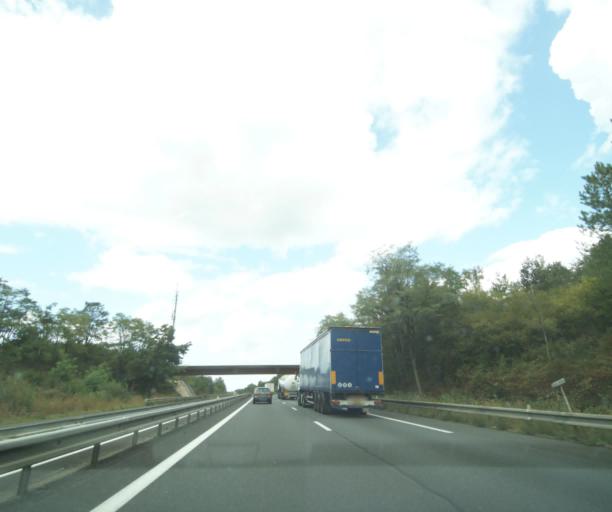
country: FR
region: Centre
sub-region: Departement du Loiret
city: La Ferte-Saint-Aubin
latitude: 47.7017
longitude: 1.9027
